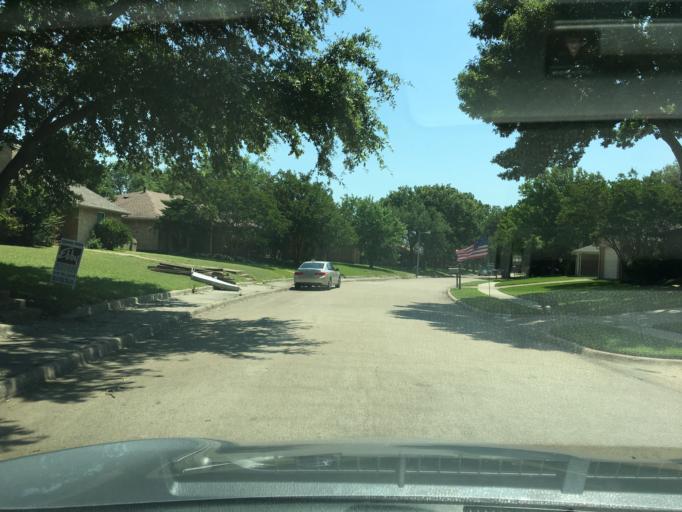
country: US
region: Texas
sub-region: Dallas County
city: Richardson
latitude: 32.9644
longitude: -96.6979
